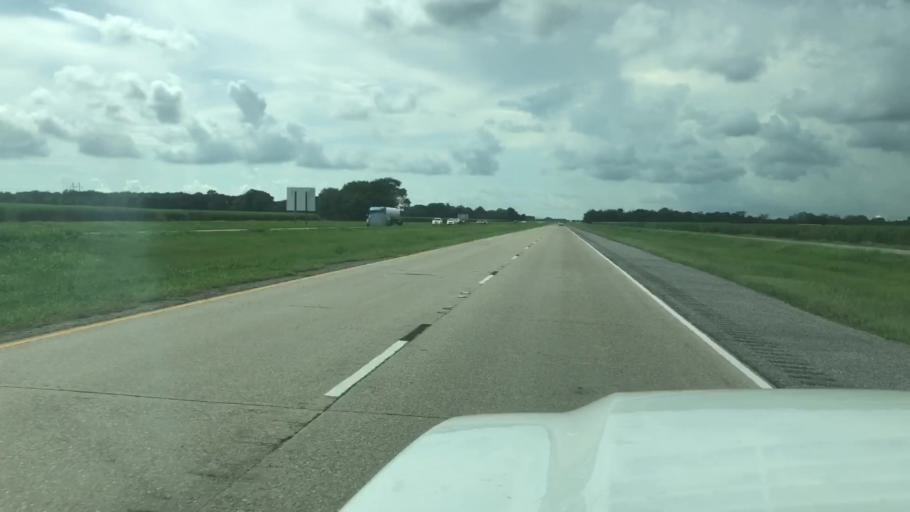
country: US
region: Louisiana
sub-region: Saint Mary Parish
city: Franklin
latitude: 29.7597
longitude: -91.4765
